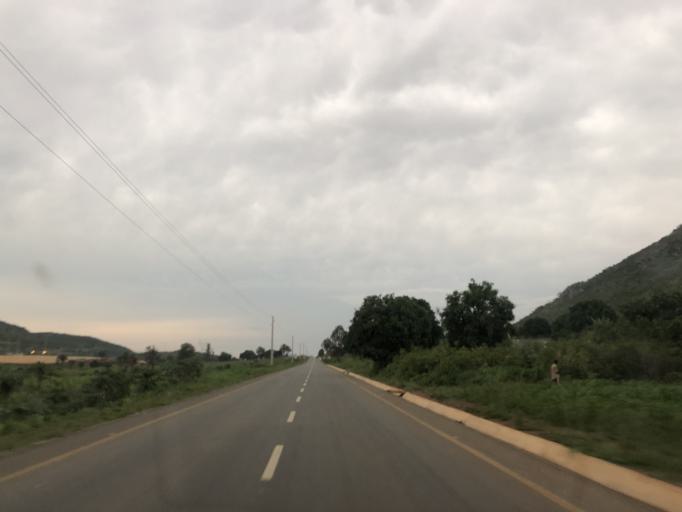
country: AO
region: Cuanza Sul
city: Uacu Cungo
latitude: -11.3184
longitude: 15.0856
